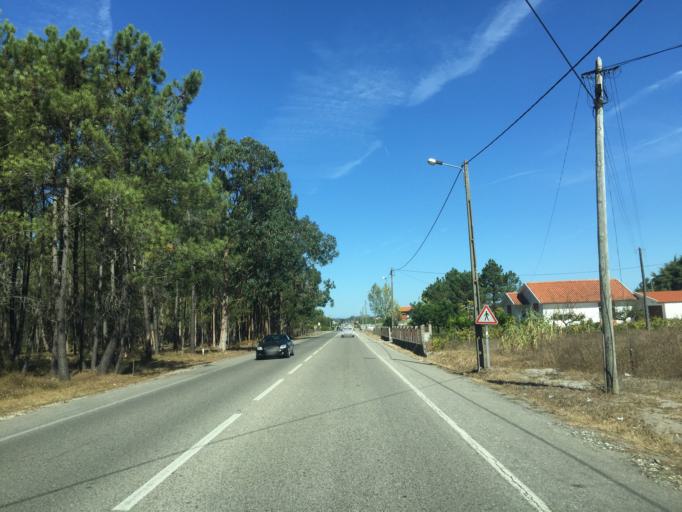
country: PT
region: Coimbra
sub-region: Figueira da Foz
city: Alhadas
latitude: 40.2240
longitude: -8.8052
